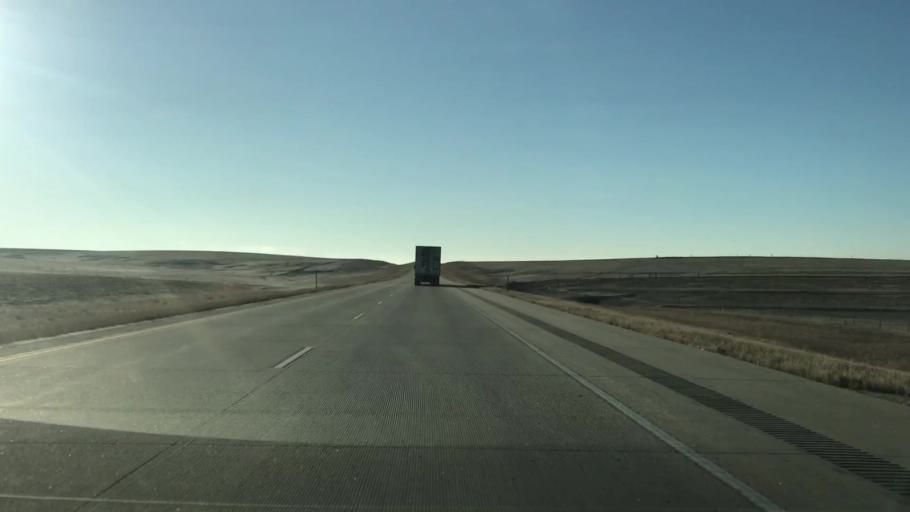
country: US
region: Colorado
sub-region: Lincoln County
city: Limon
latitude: 39.4002
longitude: -103.8990
